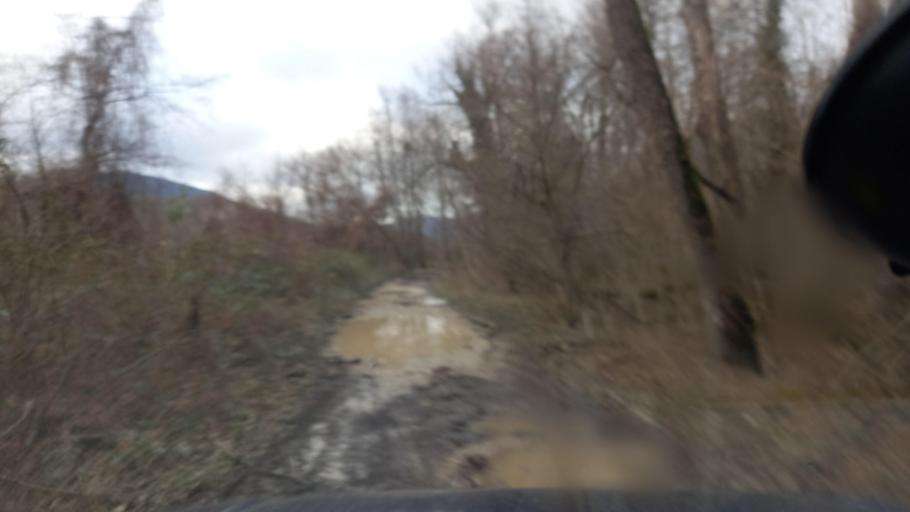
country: RU
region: Krasnodarskiy
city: Pshada
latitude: 44.4842
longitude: 38.4043
